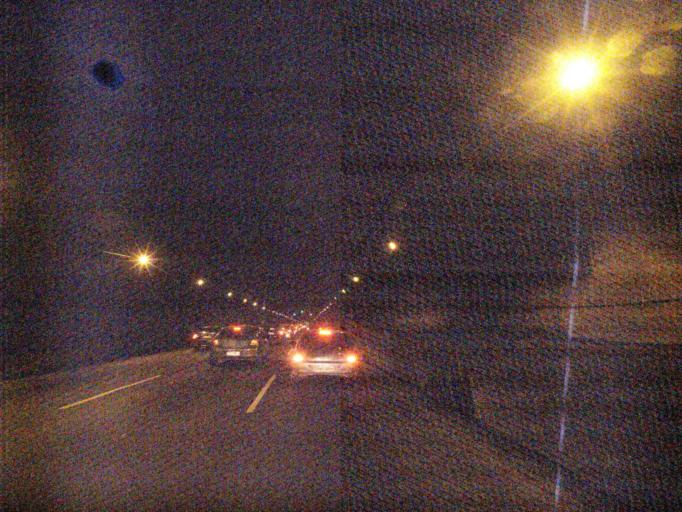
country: BR
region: Rio de Janeiro
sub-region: Rio De Janeiro
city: Rio de Janeiro
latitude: -22.9436
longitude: -43.2027
